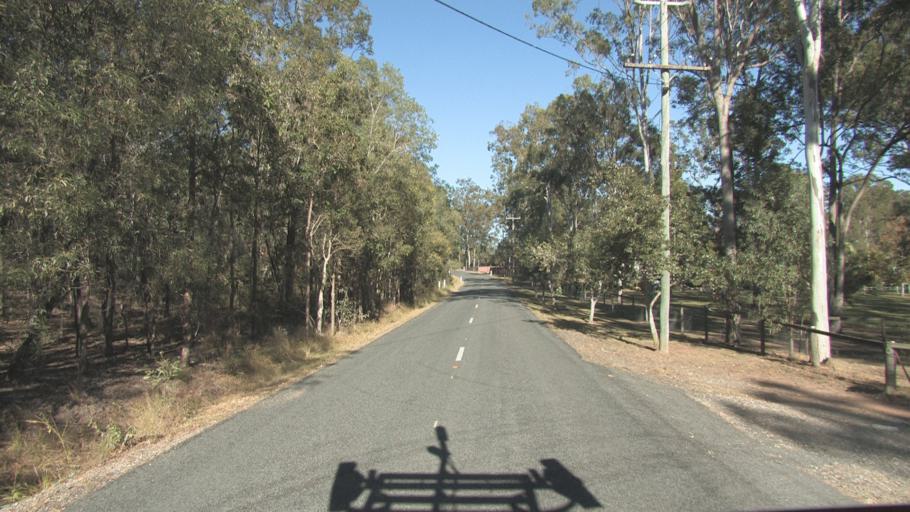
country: AU
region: Queensland
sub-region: Logan
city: North Maclean
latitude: -27.7846
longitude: 152.9635
